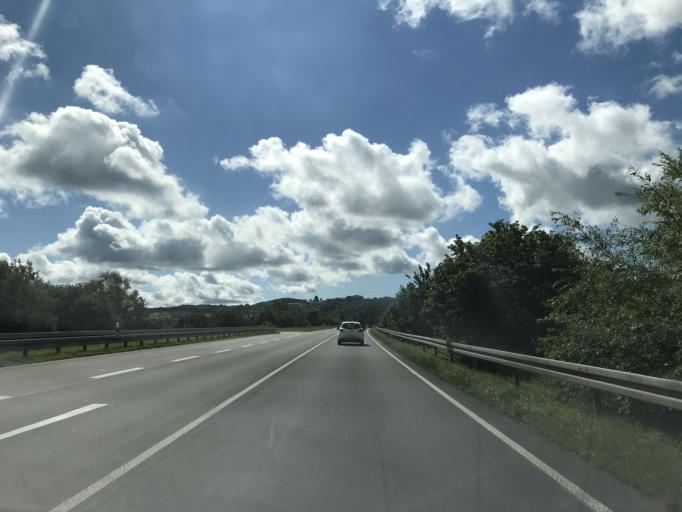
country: DE
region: Baden-Wuerttemberg
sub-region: Freiburg Region
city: Maulburg
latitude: 47.6472
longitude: 7.7927
